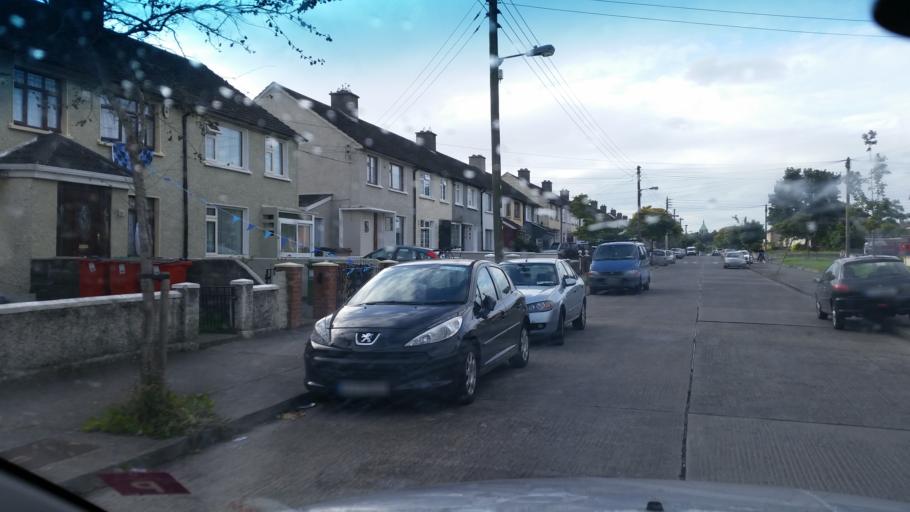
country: IE
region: Leinster
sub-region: Dublin City
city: Finglas
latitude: 53.3850
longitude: -6.2906
